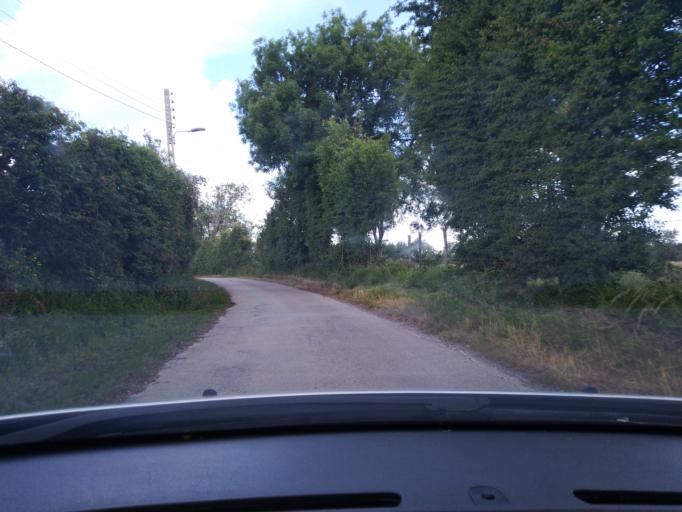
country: FR
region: Nord-Pas-de-Calais
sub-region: Departement du Pas-de-Calais
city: Ferques
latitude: 50.8359
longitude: 1.7564
